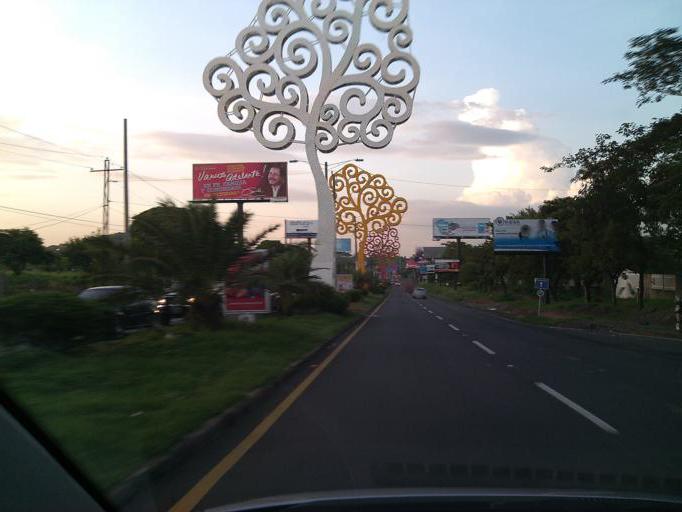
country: NI
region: Managua
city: Managua
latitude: 12.1312
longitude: -86.2669
